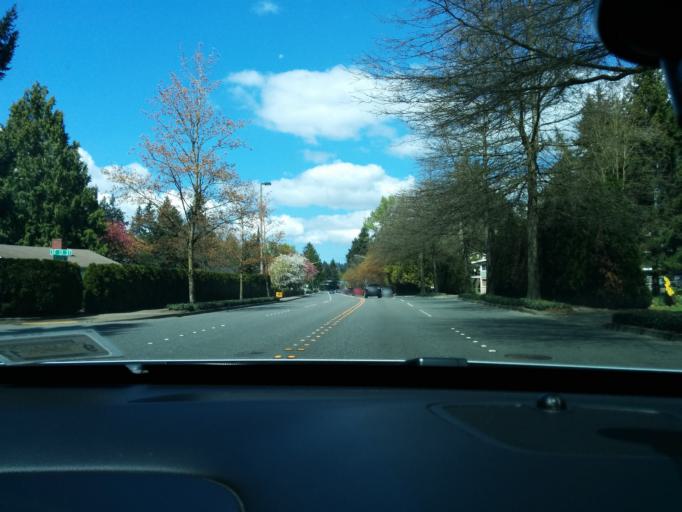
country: US
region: Washington
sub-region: King County
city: Bellevue
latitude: 47.5988
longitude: -122.1992
